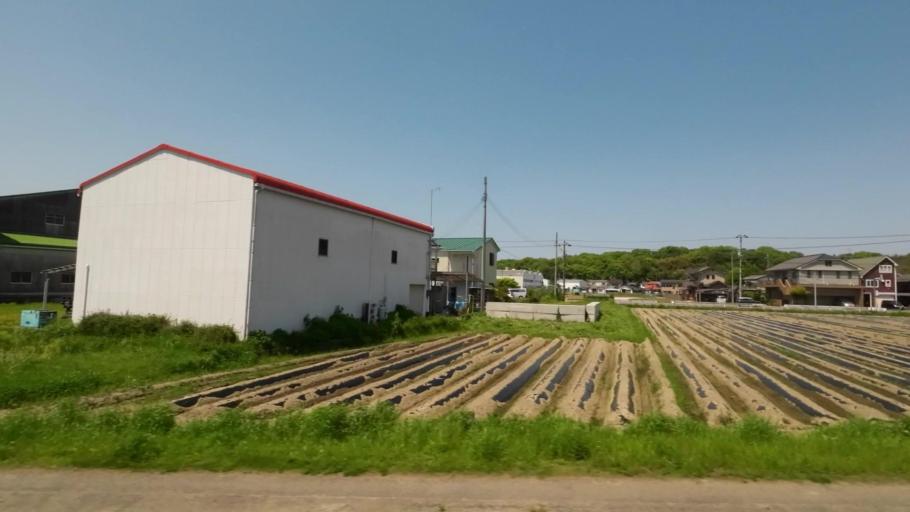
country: JP
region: Ehime
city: Hojo
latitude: 34.0769
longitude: 132.9311
